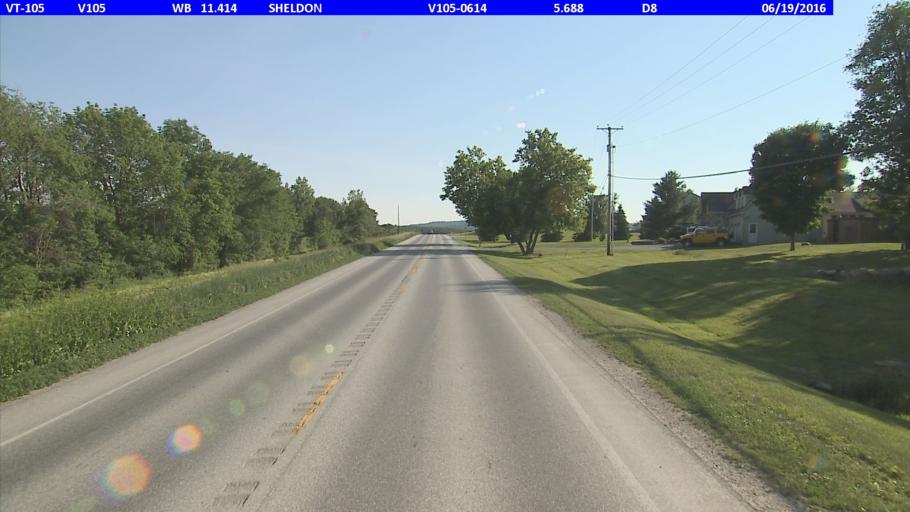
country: US
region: Vermont
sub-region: Franklin County
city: Enosburg Falls
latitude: 44.9063
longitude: -72.9244
